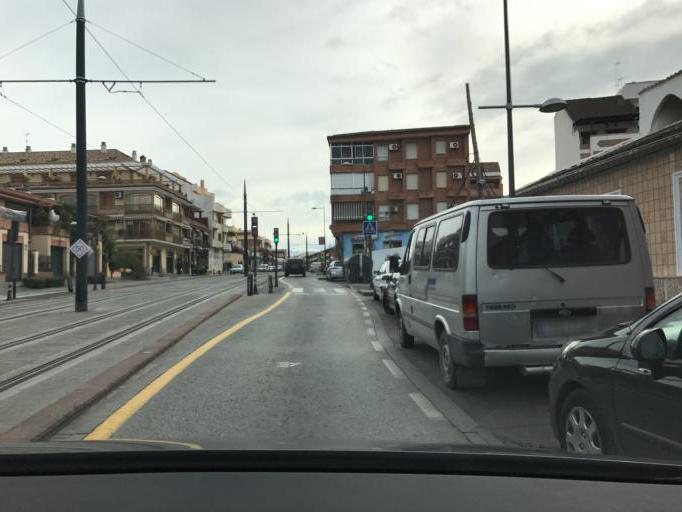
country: ES
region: Andalusia
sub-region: Provincia de Granada
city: Maracena
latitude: 37.2101
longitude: -3.6331
